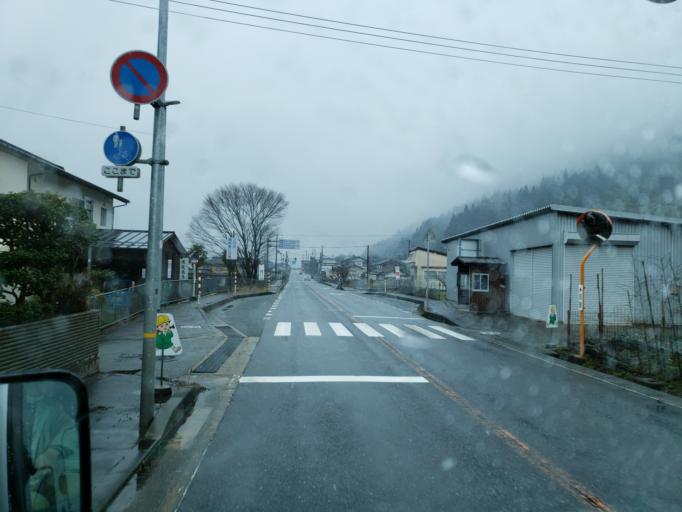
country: JP
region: Hyogo
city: Toyooka
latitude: 35.3857
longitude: 134.7209
